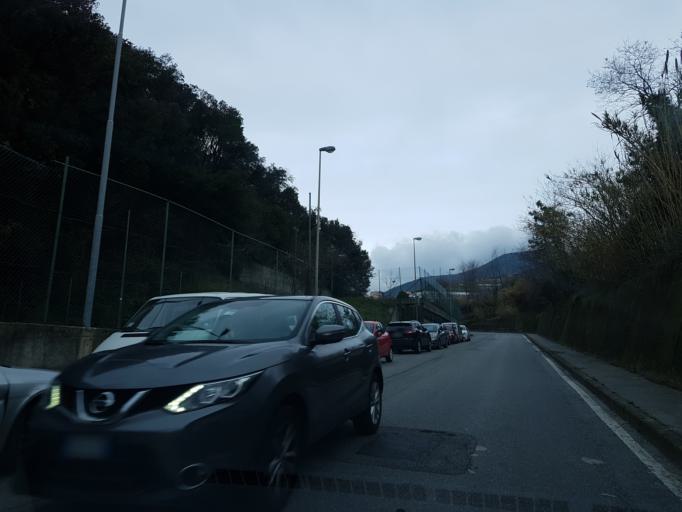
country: IT
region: Liguria
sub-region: Provincia di Genova
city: Mele
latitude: 44.4292
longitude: 8.8012
